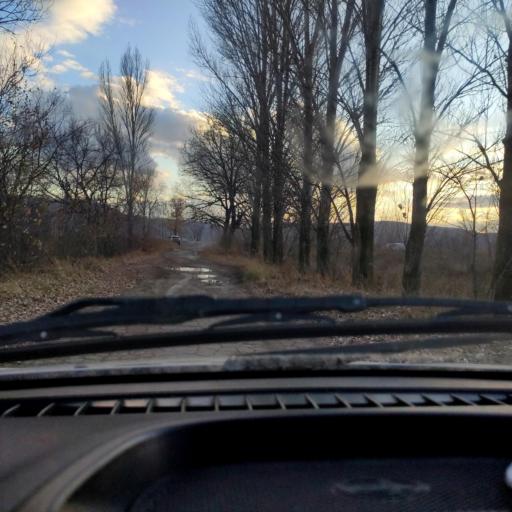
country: RU
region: Samara
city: Povolzhskiy
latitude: 53.4671
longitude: 49.6863
